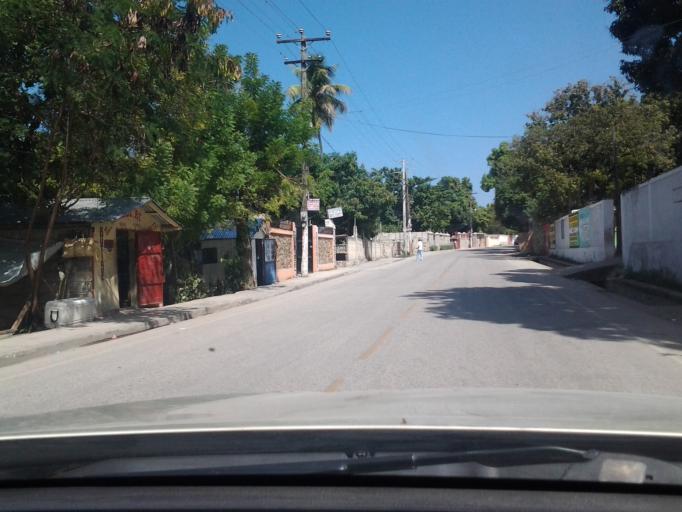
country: HT
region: Ouest
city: Tigwav
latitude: 18.4367
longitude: -72.8583
